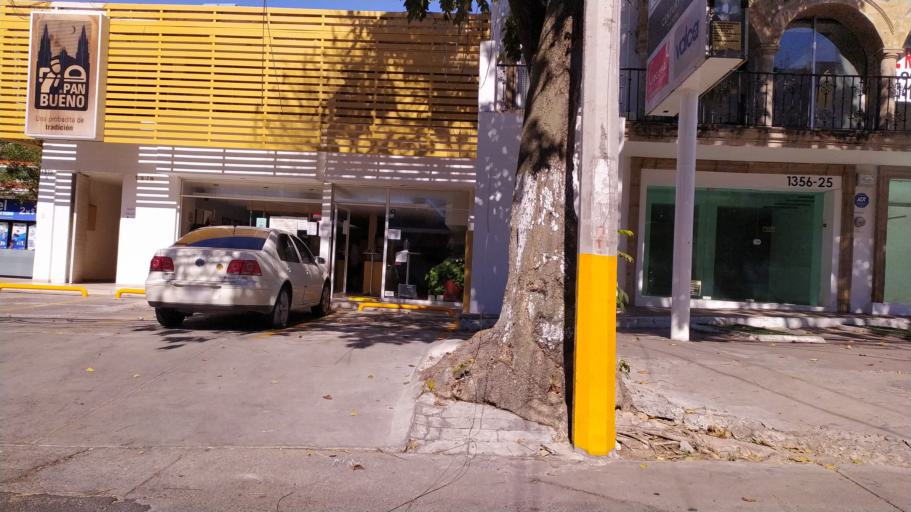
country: MX
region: Jalisco
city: Zapopan2
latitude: 20.6971
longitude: -103.3828
